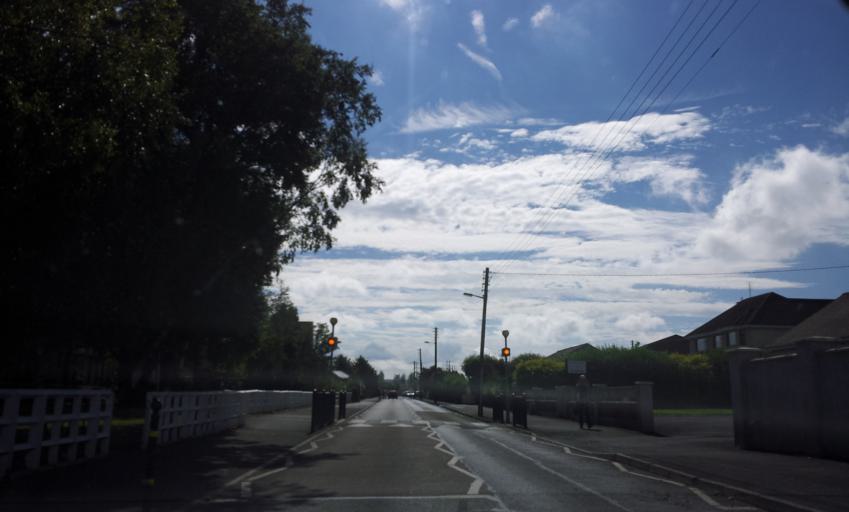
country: IE
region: Leinster
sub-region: Laois
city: Portlaoise
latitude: 53.0319
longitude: -7.2936
